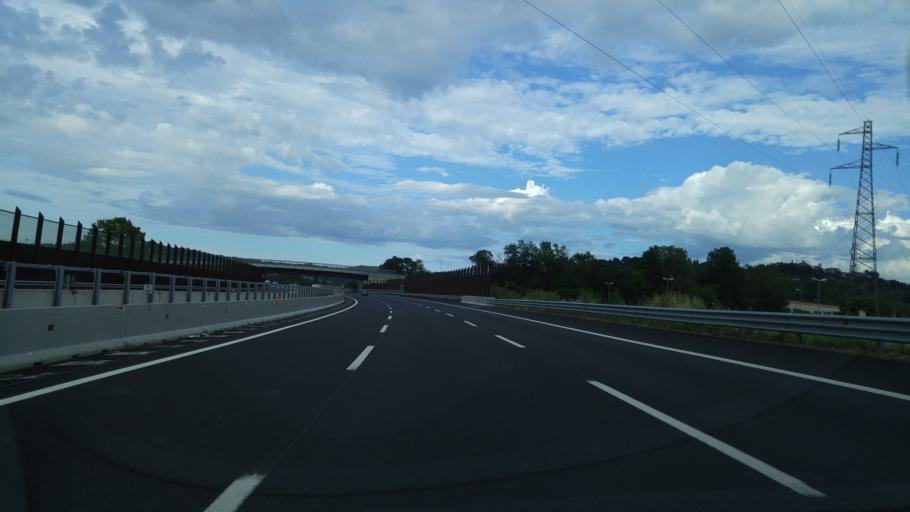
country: IT
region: Emilia-Romagna
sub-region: Provincia di Rimini
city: Cattolica
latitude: 43.9506
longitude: 12.7373
